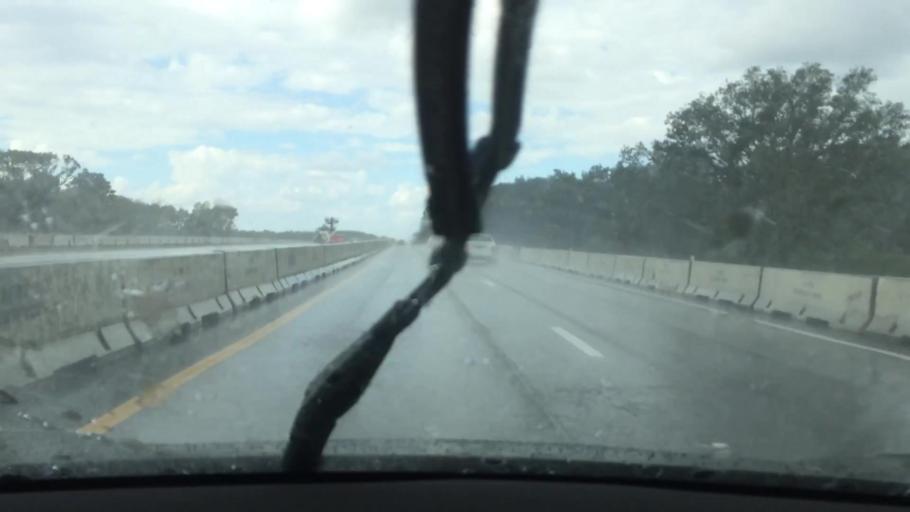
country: US
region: Florida
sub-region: Orange County
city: Wedgefield
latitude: 28.4517
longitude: -81.1045
